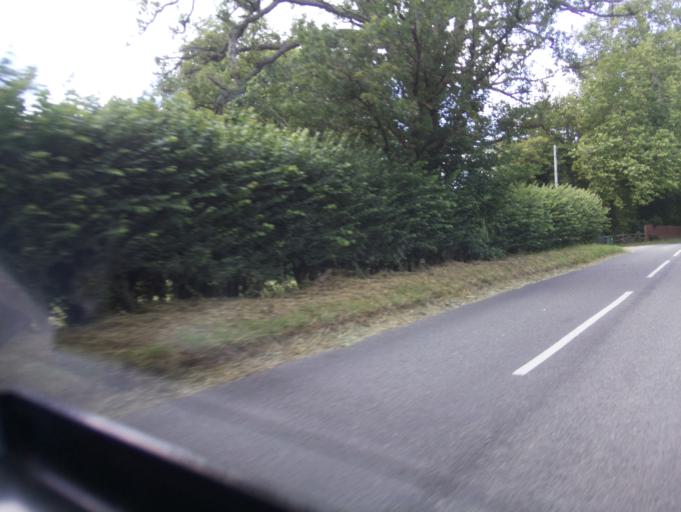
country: GB
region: England
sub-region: Oxfordshire
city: Faringdon
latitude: 51.6292
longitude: -1.5851
